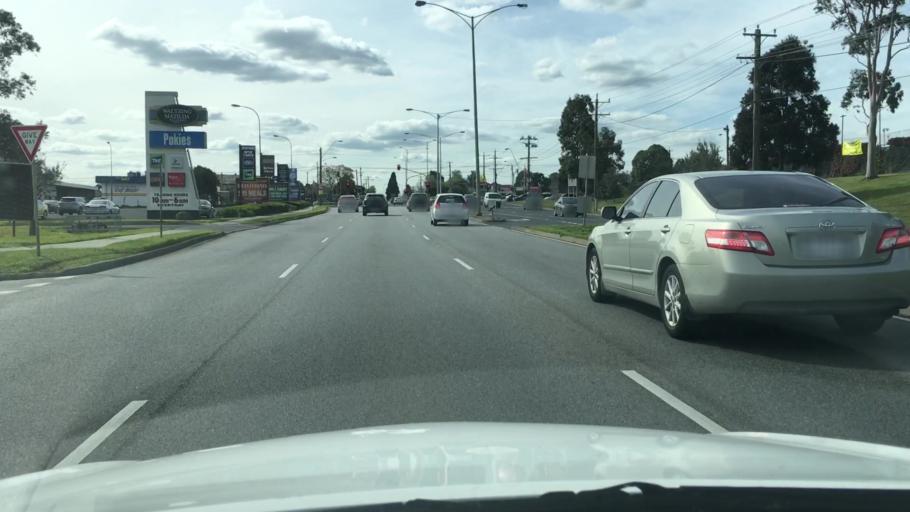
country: AU
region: Victoria
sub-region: Greater Dandenong
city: Springvale South
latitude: -37.9638
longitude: 145.1499
